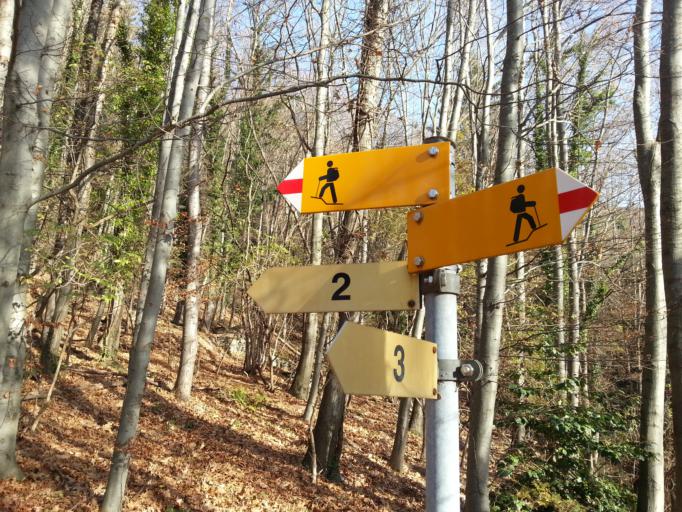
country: IT
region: Lombardy
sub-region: Provincia di Como
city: Maslianico
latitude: 45.8578
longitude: 9.0467
